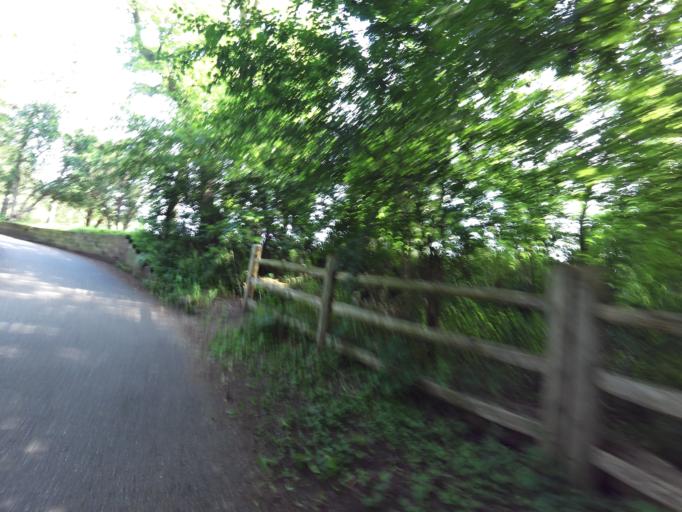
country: CA
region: Ontario
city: Etobicoke
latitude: 43.6720
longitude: -79.5129
